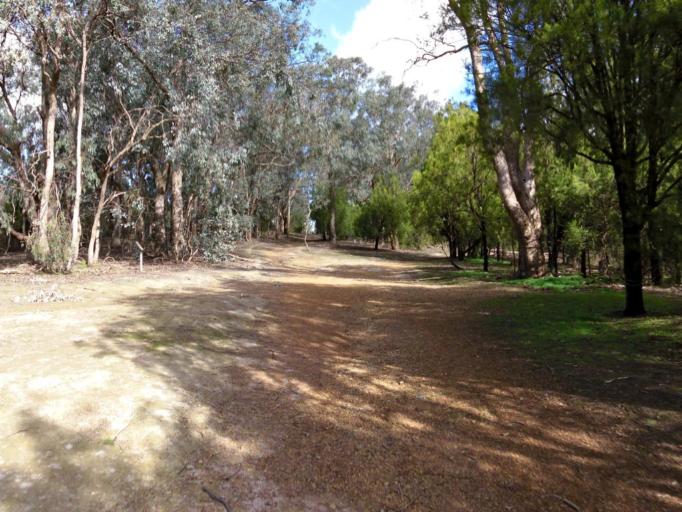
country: AU
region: Victoria
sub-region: Manningham
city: Park Orchards
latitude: -37.7748
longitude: 145.2267
